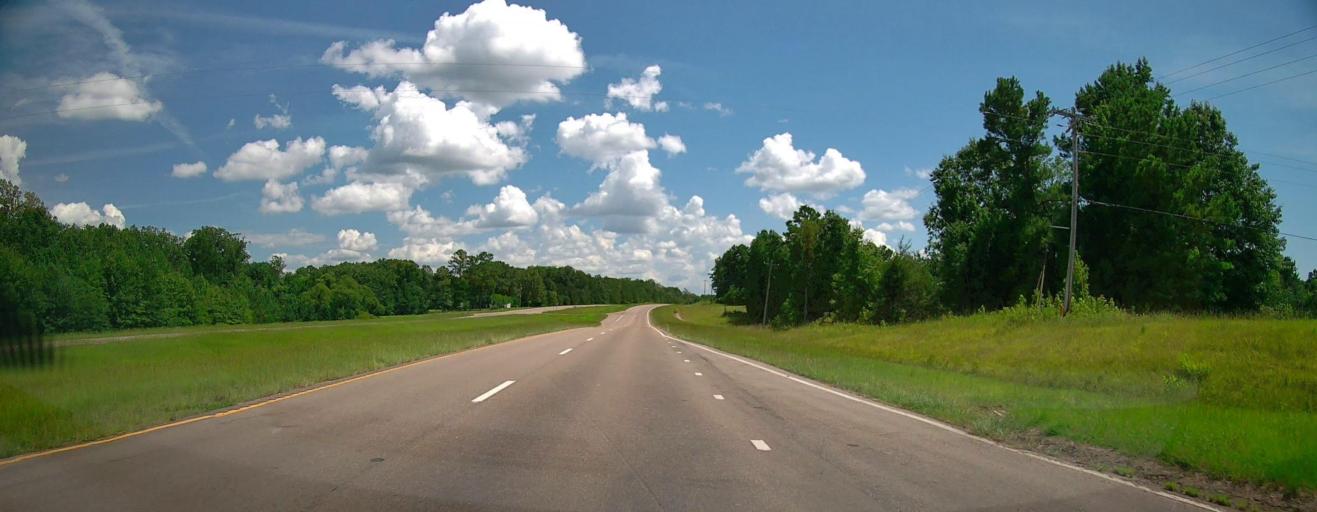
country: US
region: Mississippi
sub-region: Monroe County
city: Amory
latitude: 33.9426
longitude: -88.5994
